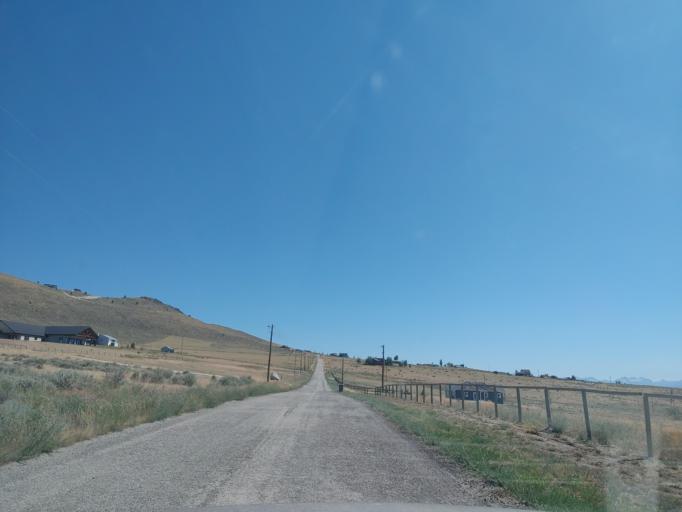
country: US
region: Montana
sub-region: Ravalli County
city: Hamilton
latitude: 46.3555
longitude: -114.0378
